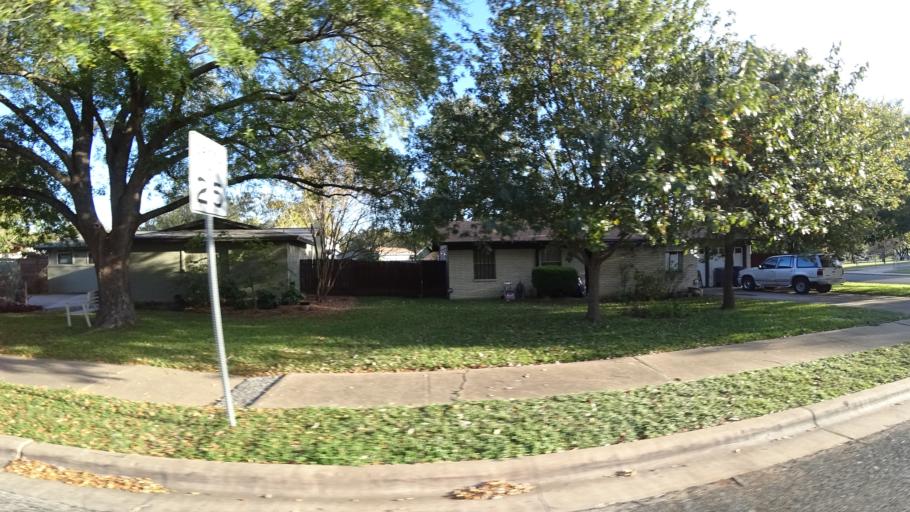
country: US
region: Texas
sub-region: Williamson County
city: Jollyville
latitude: 30.3694
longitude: -97.7322
